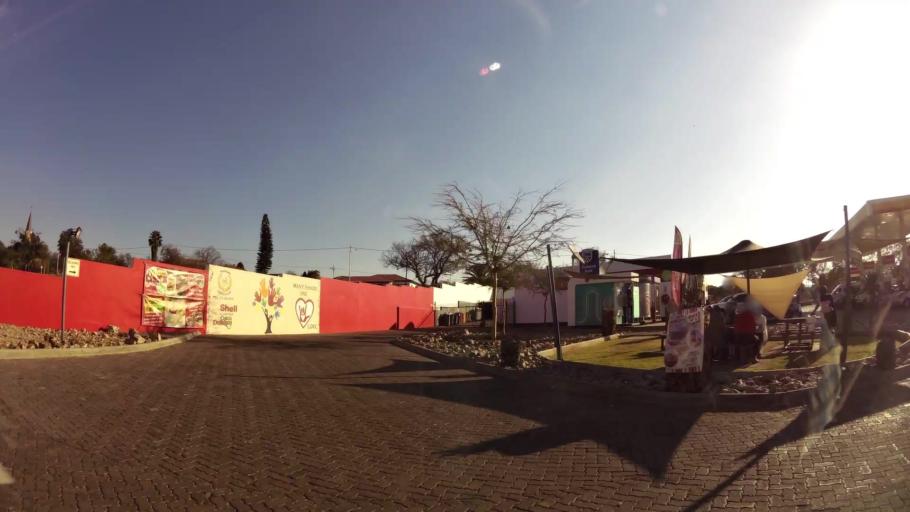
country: ZA
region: Gauteng
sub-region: City of Tshwane Metropolitan Municipality
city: Pretoria
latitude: -25.7508
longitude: 28.1328
